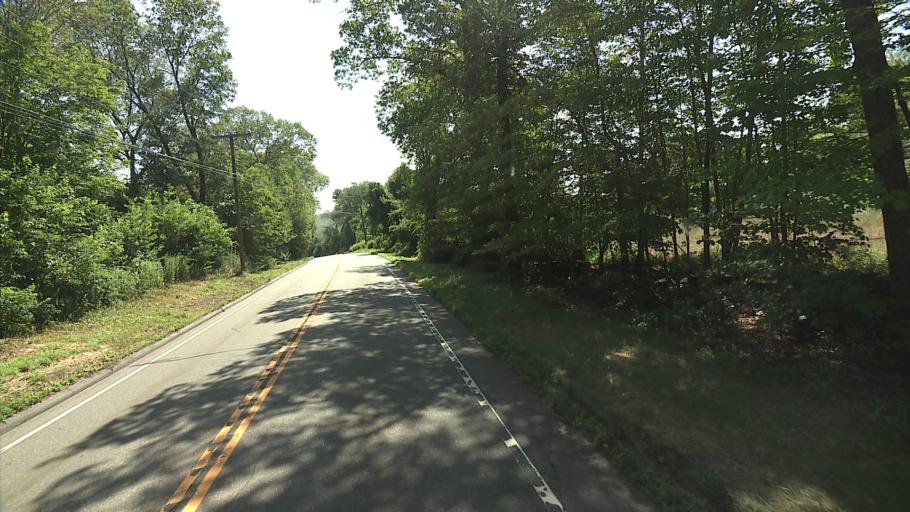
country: US
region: Connecticut
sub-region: New London County
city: Baltic
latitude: 41.6988
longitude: -72.0658
